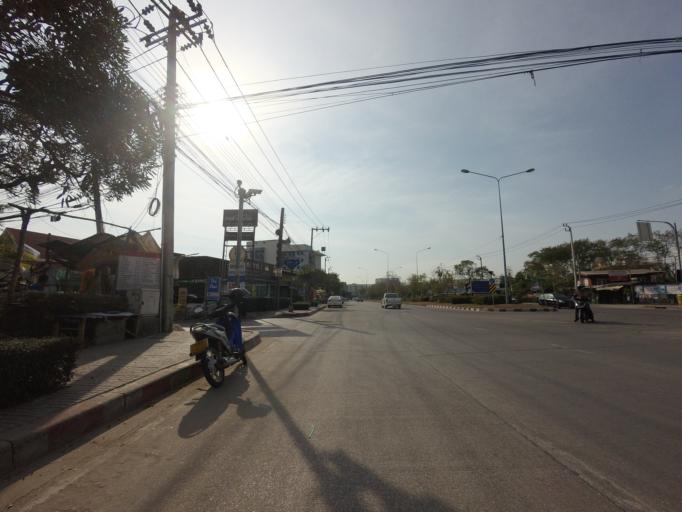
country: TH
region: Bangkok
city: Bang Kapi
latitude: 13.7520
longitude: 100.6355
